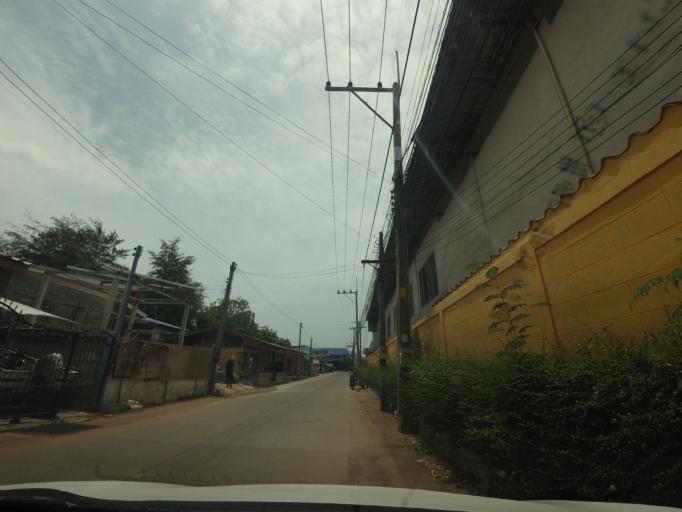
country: TH
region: Chon Buri
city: Sattahip
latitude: 12.6032
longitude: 100.9540
